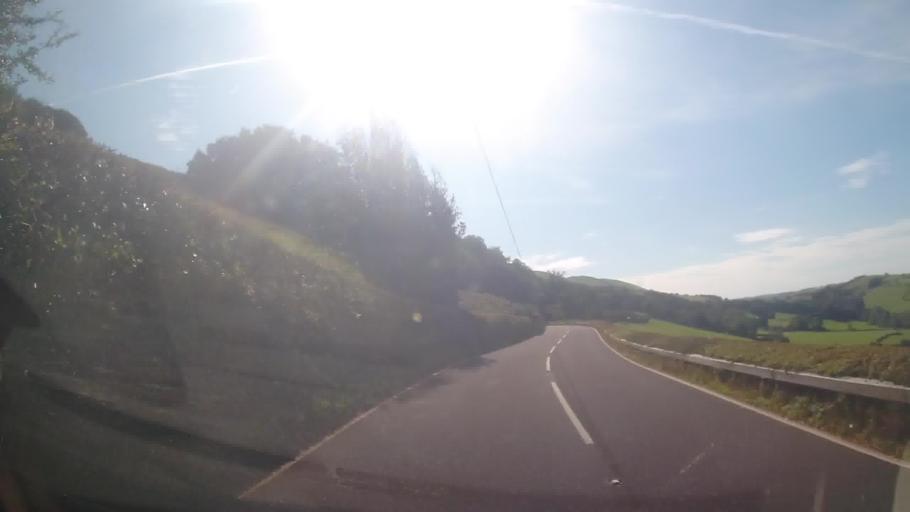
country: GB
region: Wales
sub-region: Sir Powys
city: Mochdre
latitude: 52.4704
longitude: -3.3196
